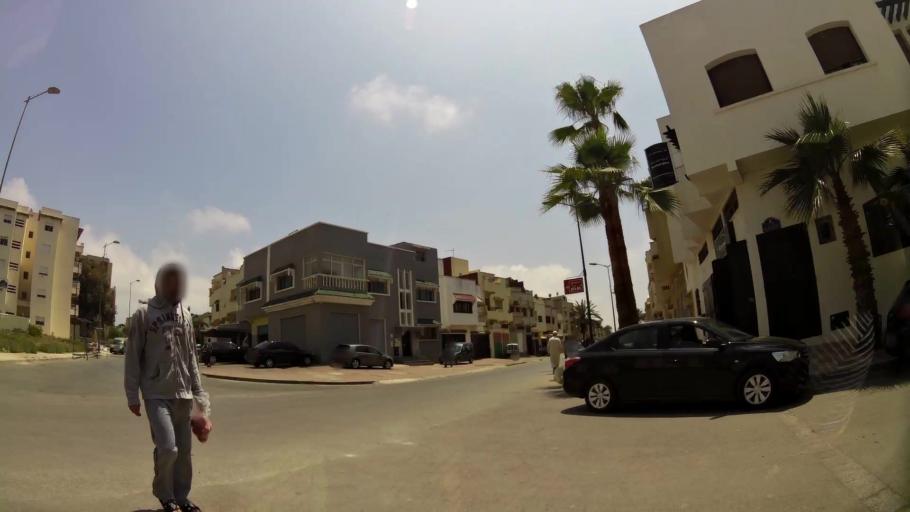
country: MA
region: Rabat-Sale-Zemmour-Zaer
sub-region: Skhirate-Temara
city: Temara
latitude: 33.9754
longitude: -6.8970
